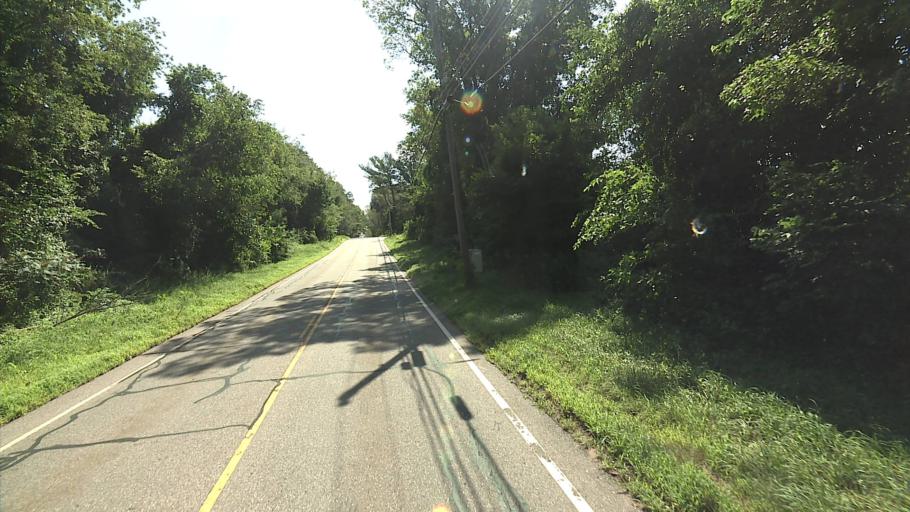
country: US
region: Connecticut
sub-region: Windham County
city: Windham
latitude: 41.6974
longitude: -72.1207
